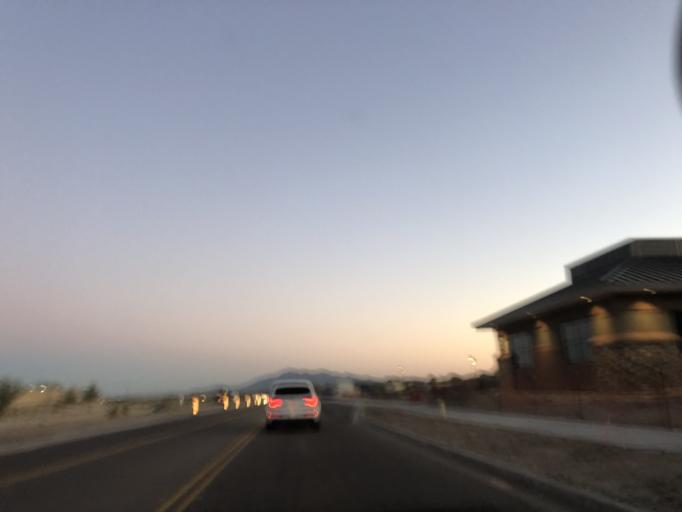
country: US
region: Arizona
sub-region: Maricopa County
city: Citrus Park
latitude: 33.4990
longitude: -112.5031
